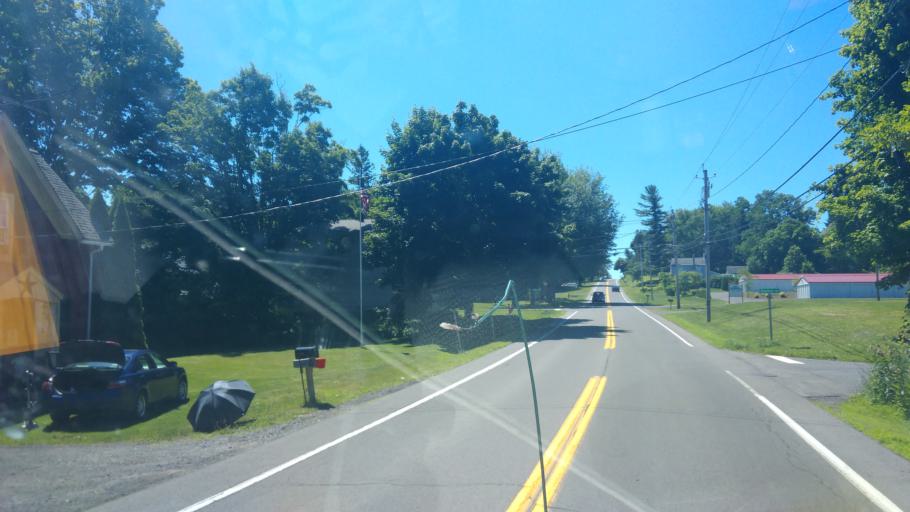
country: US
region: New York
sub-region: Wayne County
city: Sodus
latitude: 43.2606
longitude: -76.9950
